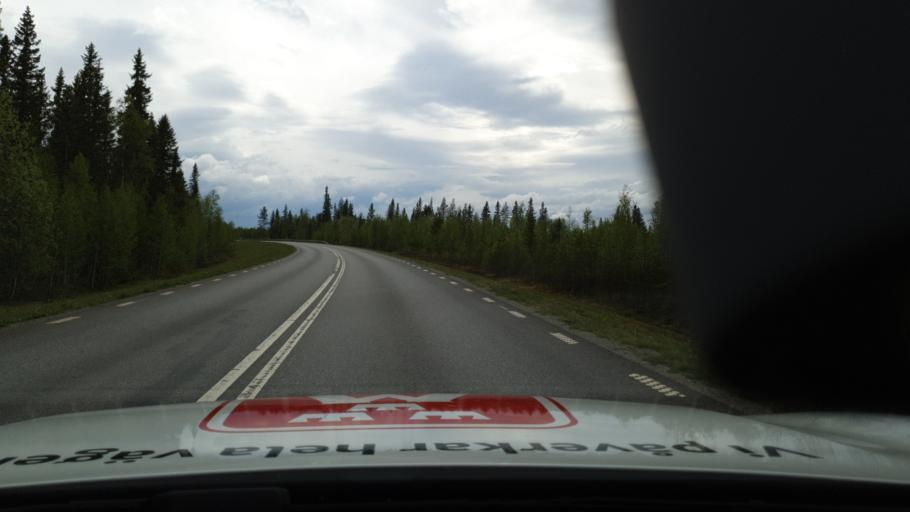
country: SE
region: Vaesterbotten
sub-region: Dorotea Kommun
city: Dorotea
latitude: 64.3410
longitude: 16.6434
